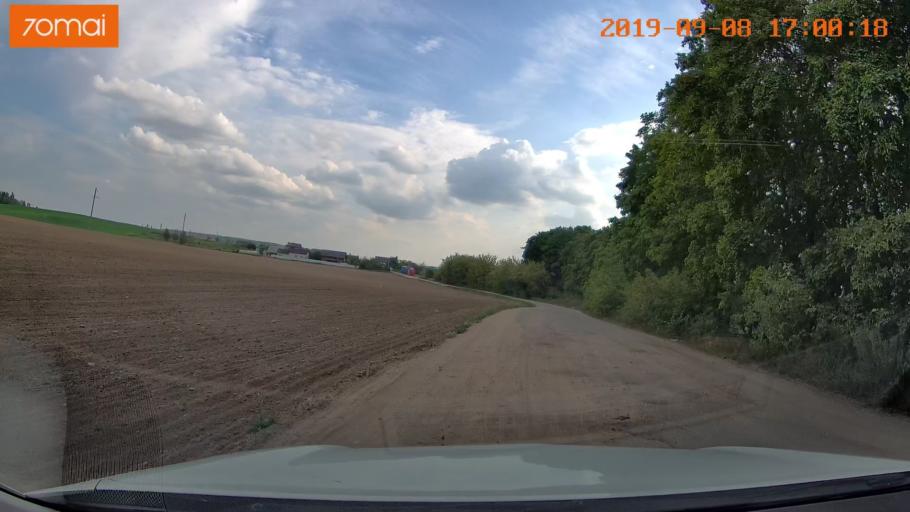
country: BY
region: Grodnenskaya
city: Hrodna
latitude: 53.7165
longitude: 23.9324
